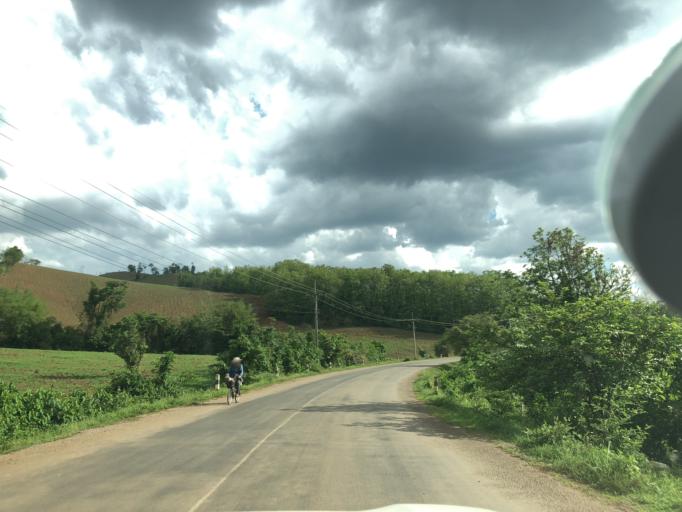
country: TH
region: Uttaradit
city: Ban Khok
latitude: 18.1290
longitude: 101.3761
